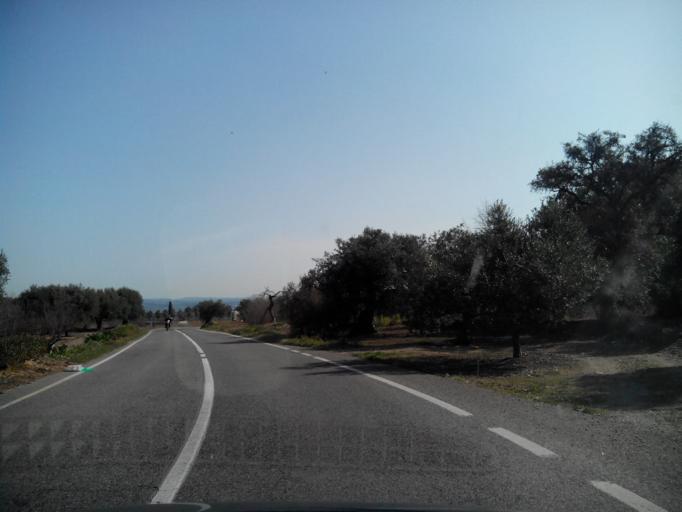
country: ES
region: Catalonia
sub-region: Provincia de Tarragona
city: La Selva
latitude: 41.2137
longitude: 1.1586
